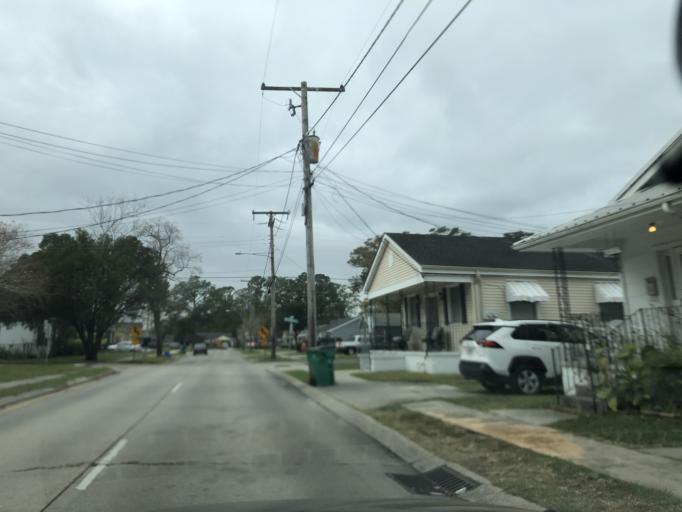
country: US
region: Louisiana
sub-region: Jefferson Parish
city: Metairie Terrace
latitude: 29.9822
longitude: -90.1626
